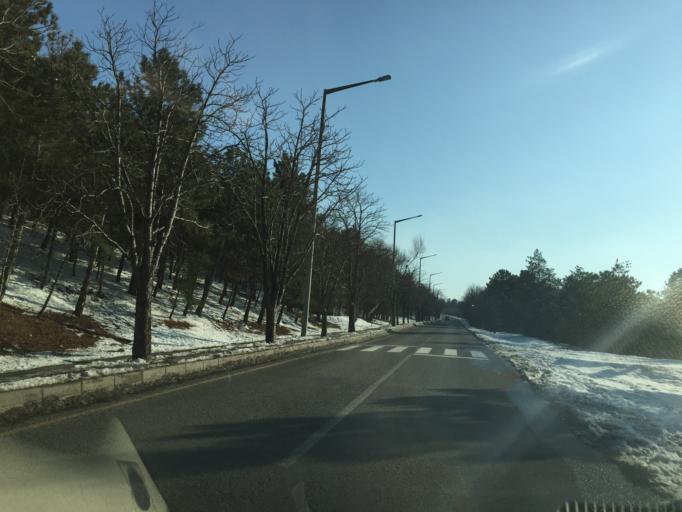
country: TR
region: Ankara
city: Ankara
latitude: 39.8944
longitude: 32.7810
